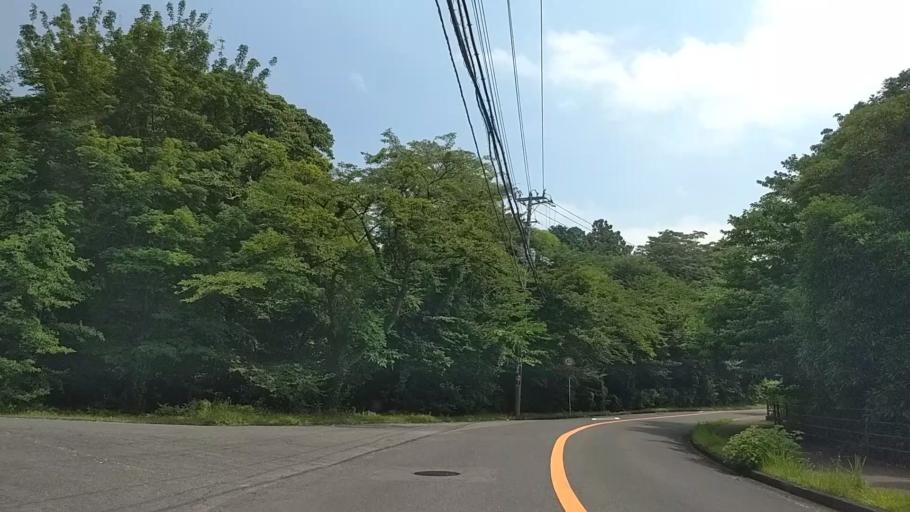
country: JP
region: Shizuoka
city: Ito
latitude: 34.9254
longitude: 139.1068
